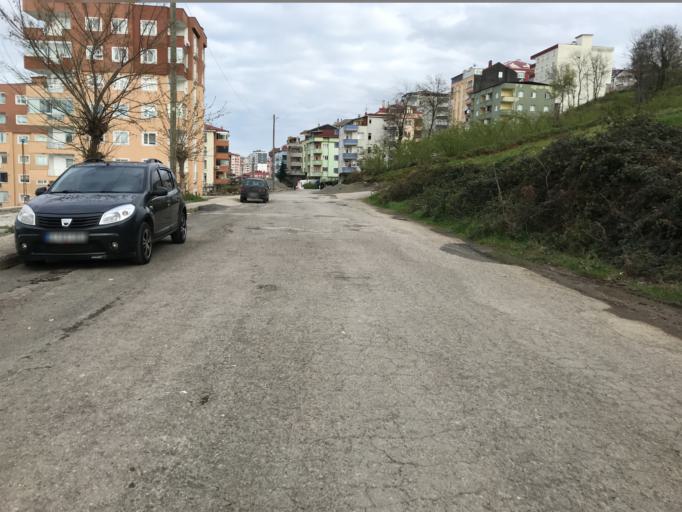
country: TR
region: Trabzon
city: Trabzon
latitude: 40.9900
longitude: 39.7794
